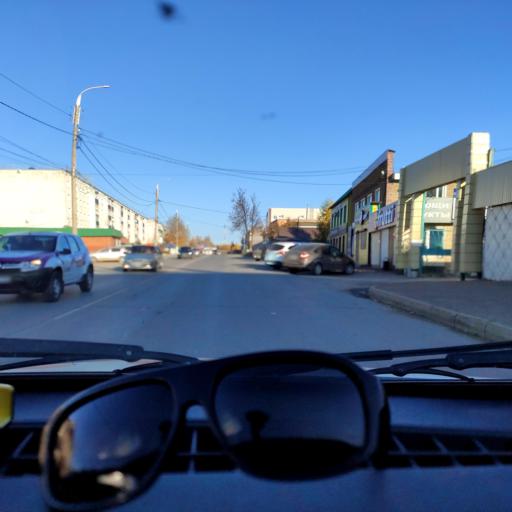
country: RU
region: Bashkortostan
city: Blagoveshchensk
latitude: 55.0469
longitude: 55.9577
